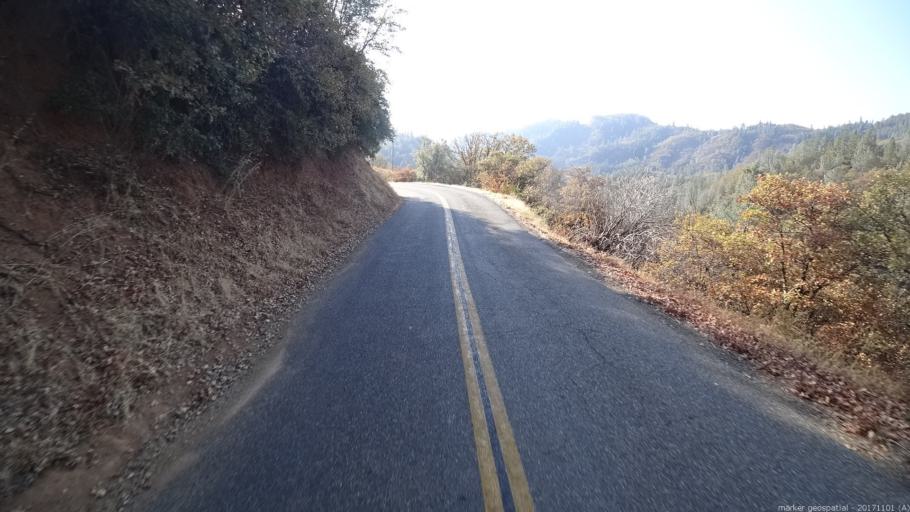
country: US
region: California
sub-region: Shasta County
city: Shasta Lake
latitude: 40.8043
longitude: -122.3180
